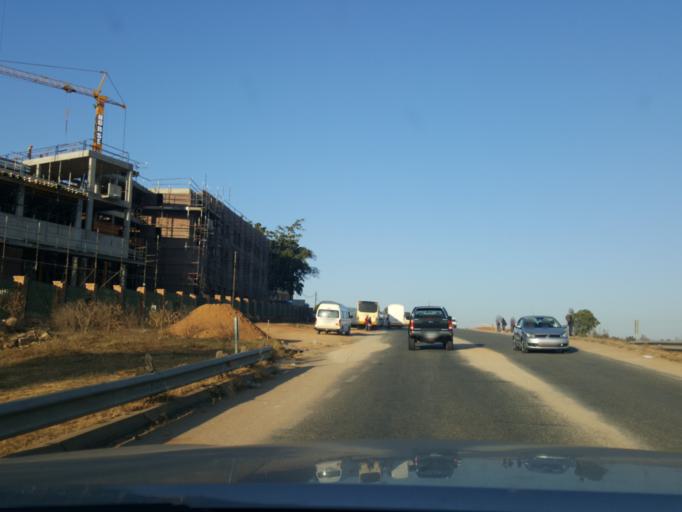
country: ZA
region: Mpumalanga
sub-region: Ehlanzeni District
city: Nelspruit
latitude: -25.4374
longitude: 30.9800
